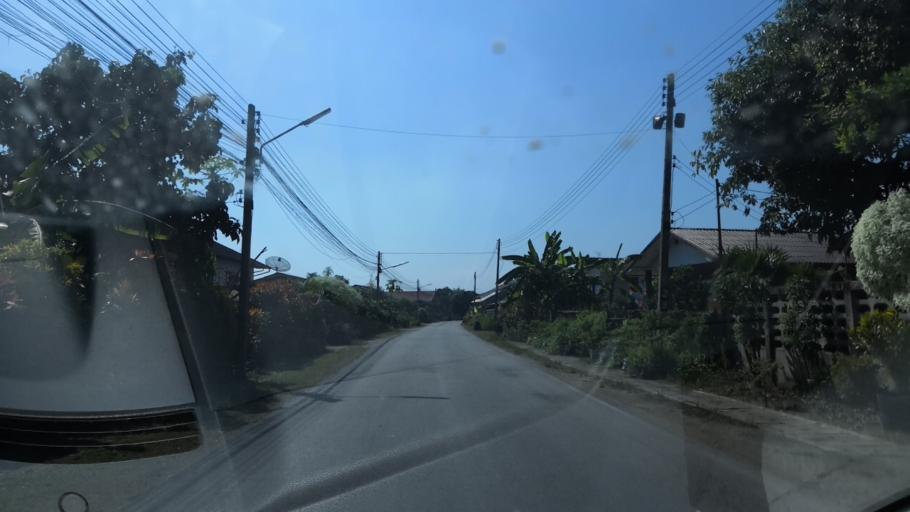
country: TH
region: Chiang Rai
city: Wiang Chai
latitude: 19.8883
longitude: 99.9492
